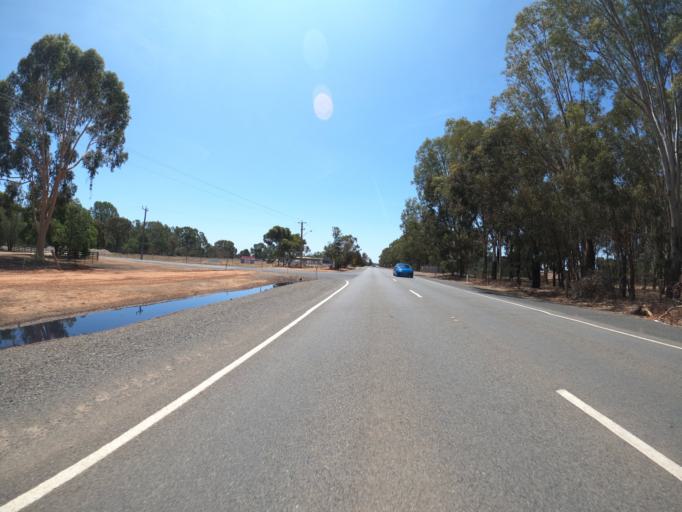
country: AU
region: Victoria
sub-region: Moira
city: Yarrawonga
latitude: -36.0365
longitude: 145.9955
